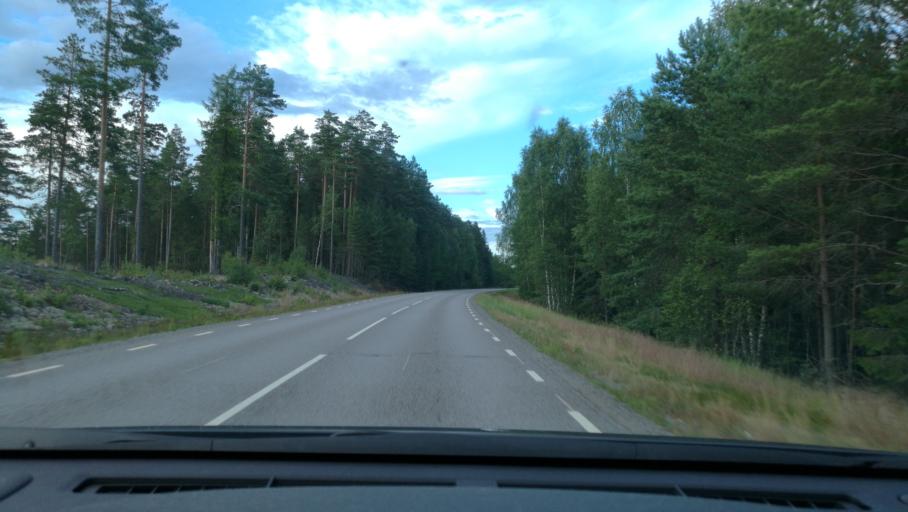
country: SE
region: OEstergoetland
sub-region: Norrkopings Kommun
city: Svartinge
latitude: 58.7400
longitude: 15.9603
